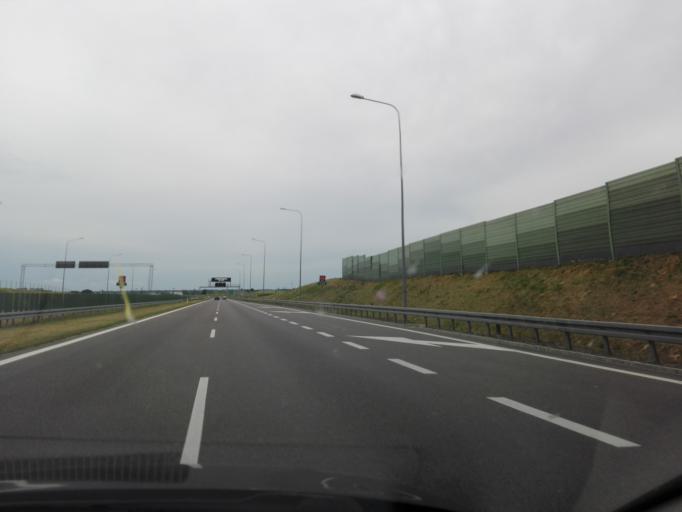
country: PL
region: Lublin Voivodeship
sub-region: Powiat lubelski
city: Jastkow
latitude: 51.3256
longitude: 22.3867
